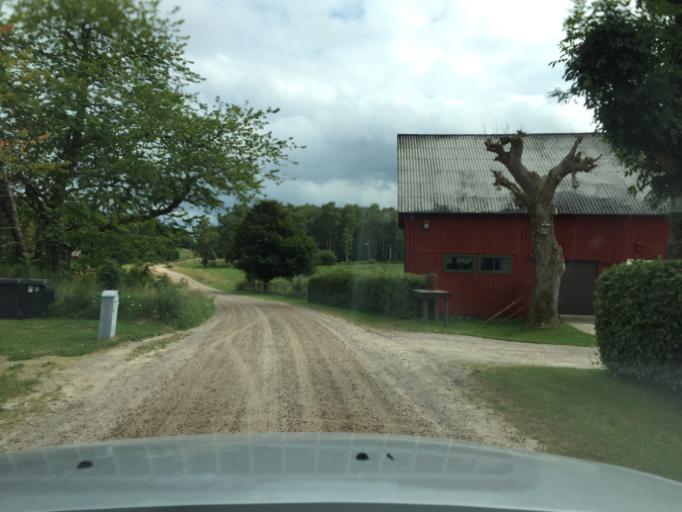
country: SE
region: Skane
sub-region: Hassleholms Kommun
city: Sosdala
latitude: 56.0191
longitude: 13.6753
